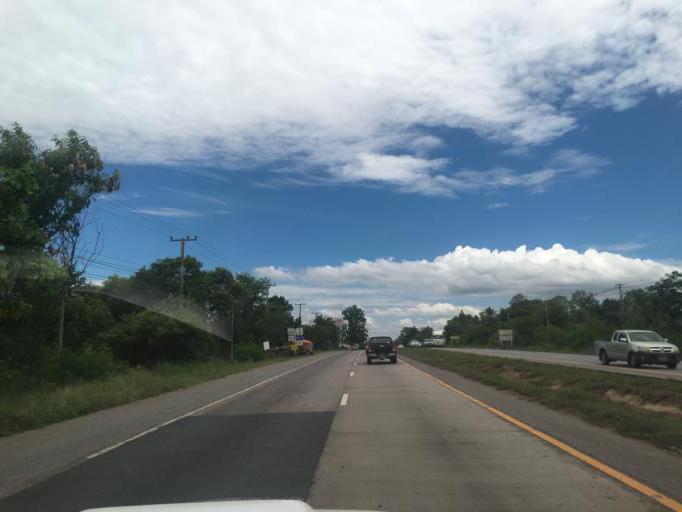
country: TH
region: Khon Kaen
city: Nam Phong
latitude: 16.6461
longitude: 102.8002
